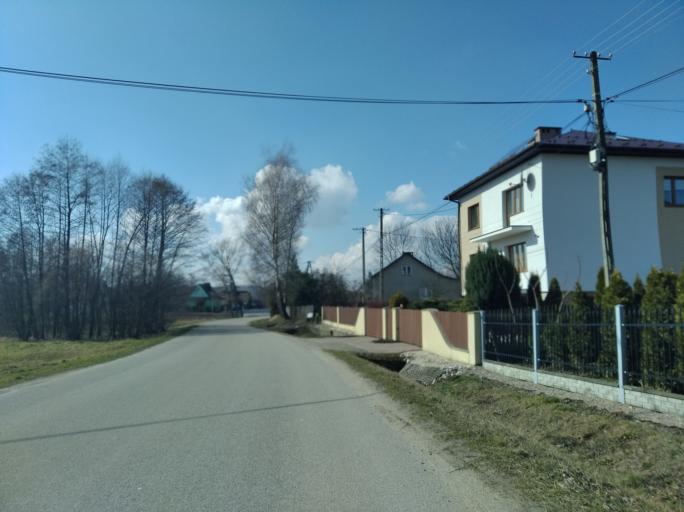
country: PL
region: Subcarpathian Voivodeship
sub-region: Powiat debicki
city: Brzostek
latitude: 49.8817
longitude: 21.4232
